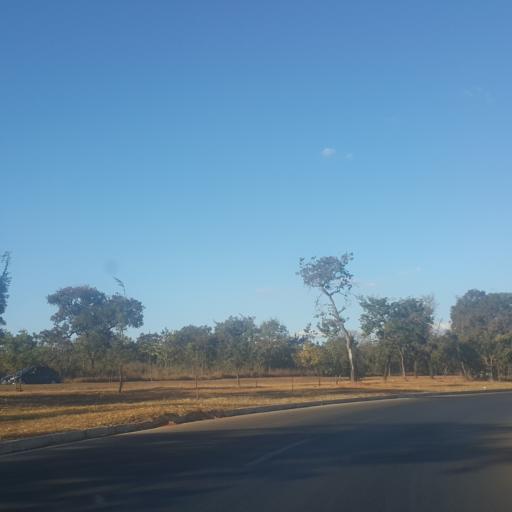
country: BR
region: Federal District
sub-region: Brasilia
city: Brasilia
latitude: -15.8288
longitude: -47.9497
